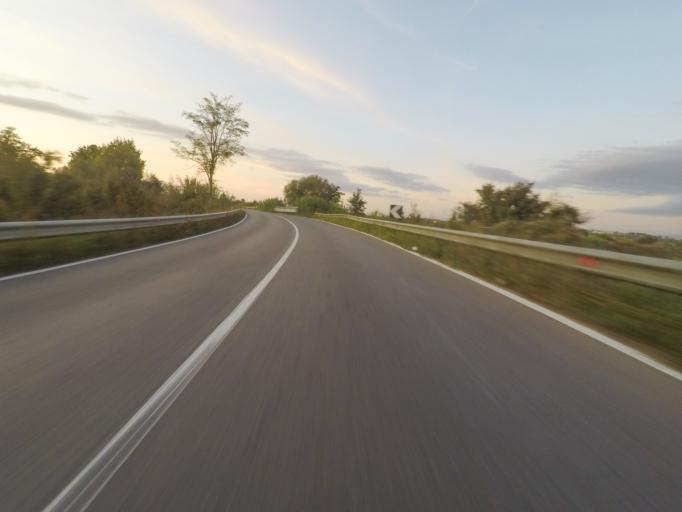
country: IT
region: Tuscany
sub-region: Provincia di Siena
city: Sinalunga
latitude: 43.1961
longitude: 11.7614
